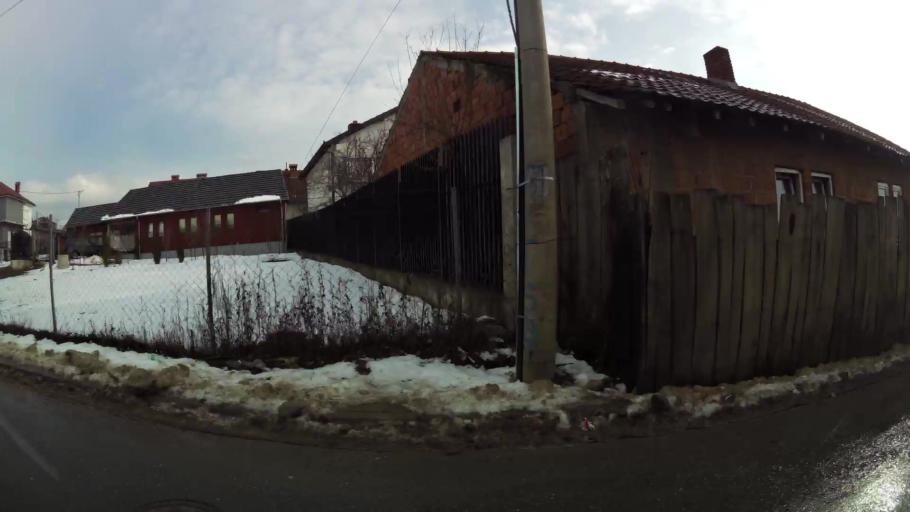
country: XK
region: Pristina
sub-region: Komuna e Prishtines
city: Pristina
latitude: 42.6871
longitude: 21.1655
